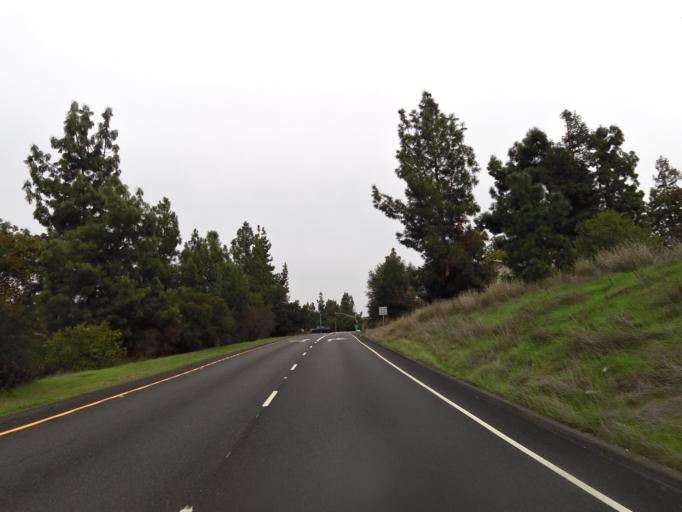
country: US
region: California
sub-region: Yolo County
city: Davis
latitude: 38.5596
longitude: -121.7674
